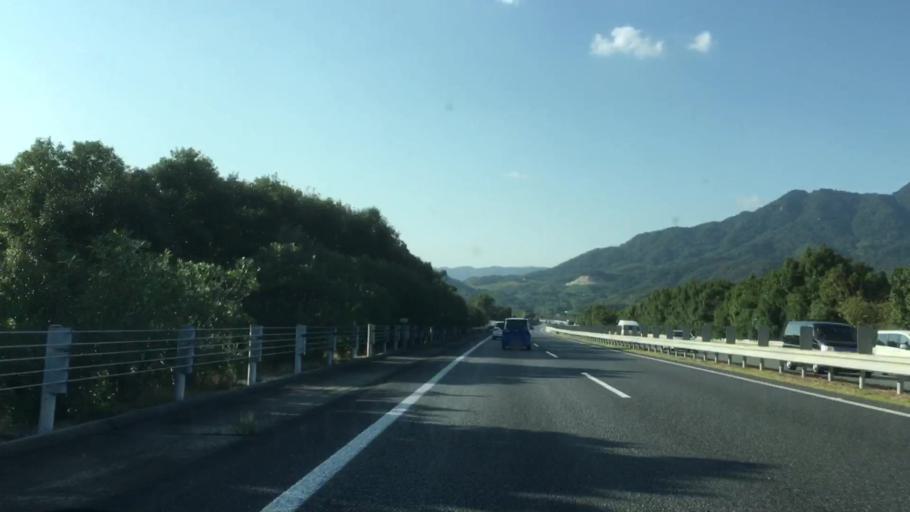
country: JP
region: Yamaguchi
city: Hofu
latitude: 34.0625
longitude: 131.6082
